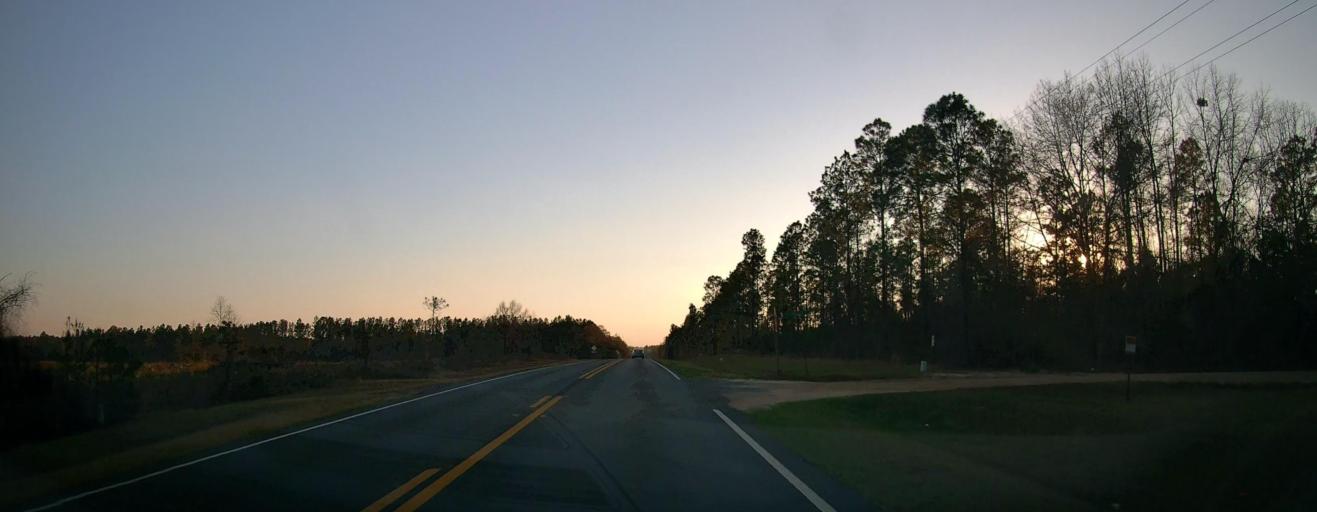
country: US
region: Georgia
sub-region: Laurens County
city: Dublin
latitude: 32.4106
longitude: -82.9606
